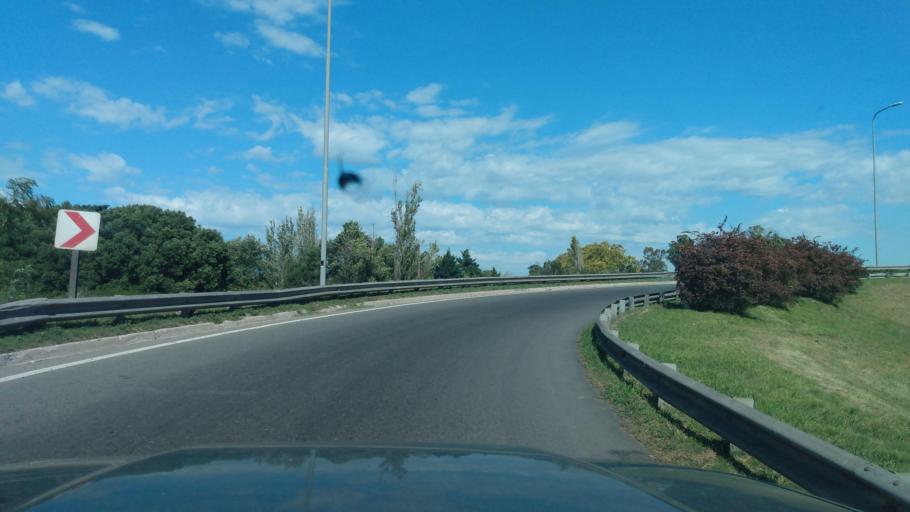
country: AR
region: Buenos Aires
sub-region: Partido de Merlo
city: Merlo
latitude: -34.6293
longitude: -58.7207
